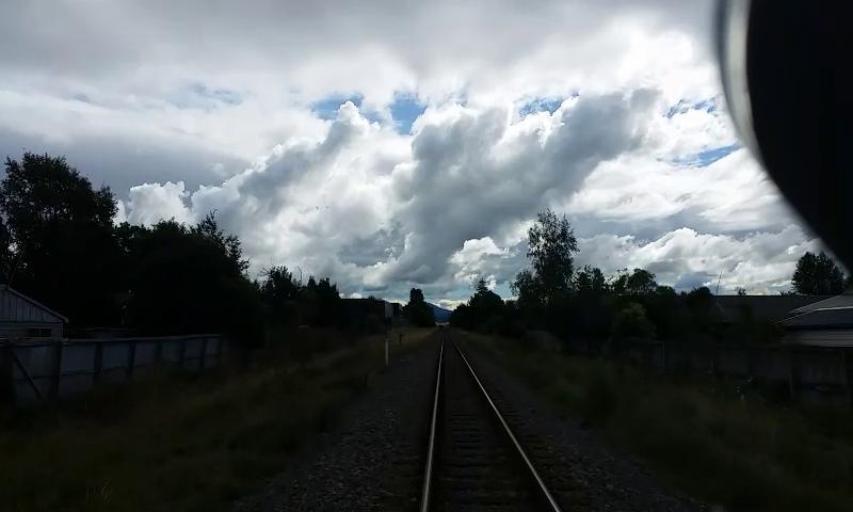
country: NZ
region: Canterbury
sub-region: Waimakariri District
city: Woodend
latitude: -43.3090
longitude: 172.5998
